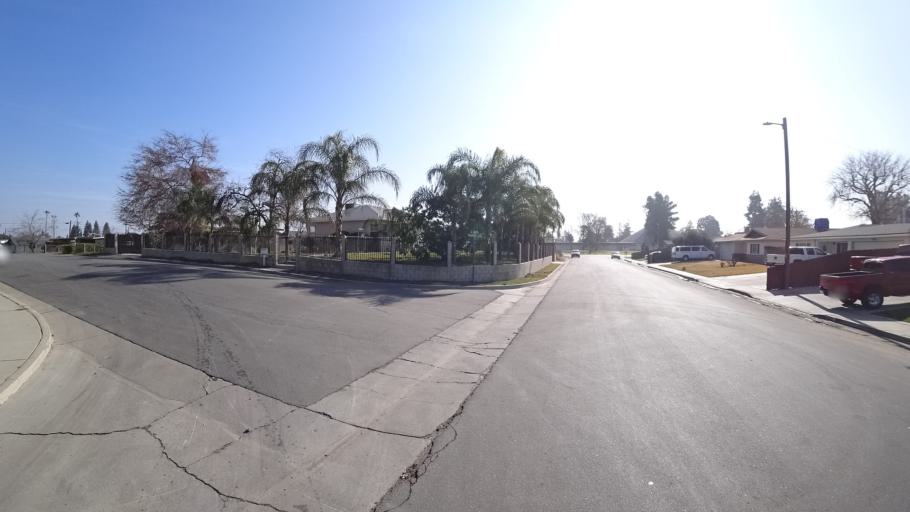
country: US
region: California
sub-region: Kern County
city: Bakersfield
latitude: 35.3333
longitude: -119.0506
